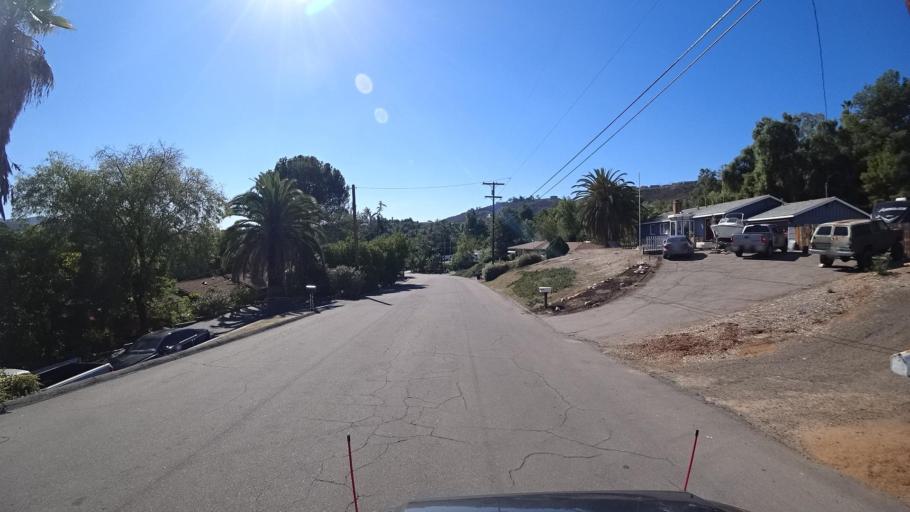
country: US
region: California
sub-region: San Diego County
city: Winter Gardens
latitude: 32.8411
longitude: -116.9404
